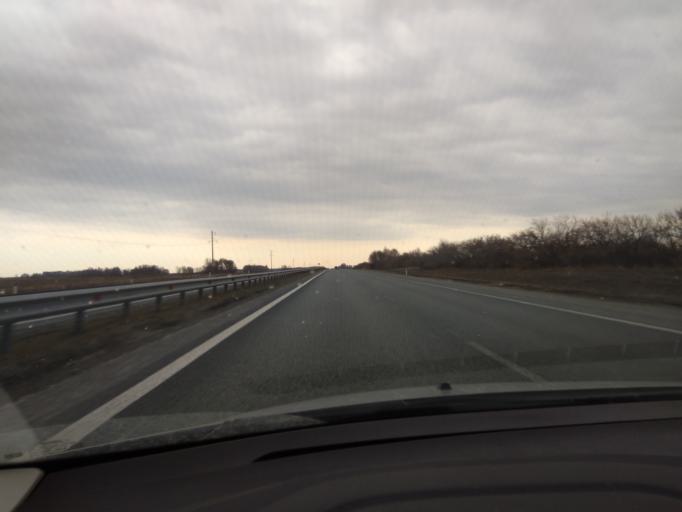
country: RU
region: Chelyabinsk
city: Kunashak
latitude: 55.7439
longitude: 61.2275
